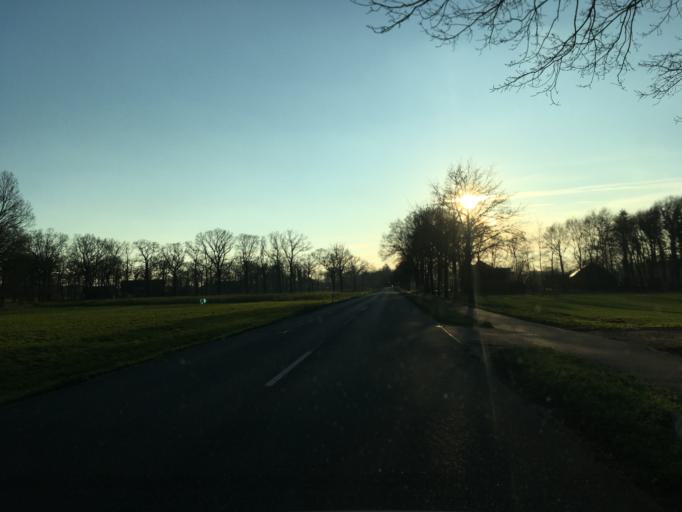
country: DE
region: North Rhine-Westphalia
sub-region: Regierungsbezirk Munster
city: Gronau
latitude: 52.1668
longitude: 7.0315
